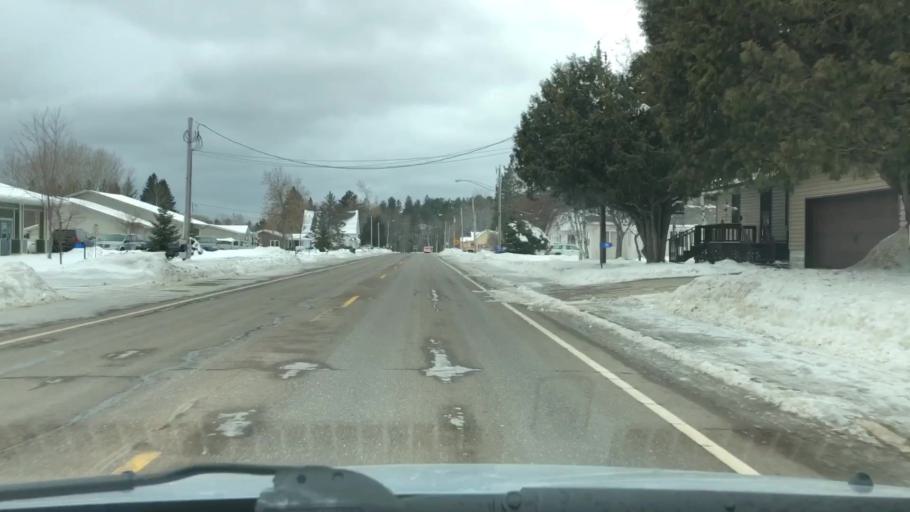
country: US
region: Minnesota
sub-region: Carlton County
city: Carlton
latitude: 46.6636
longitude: -92.3953
